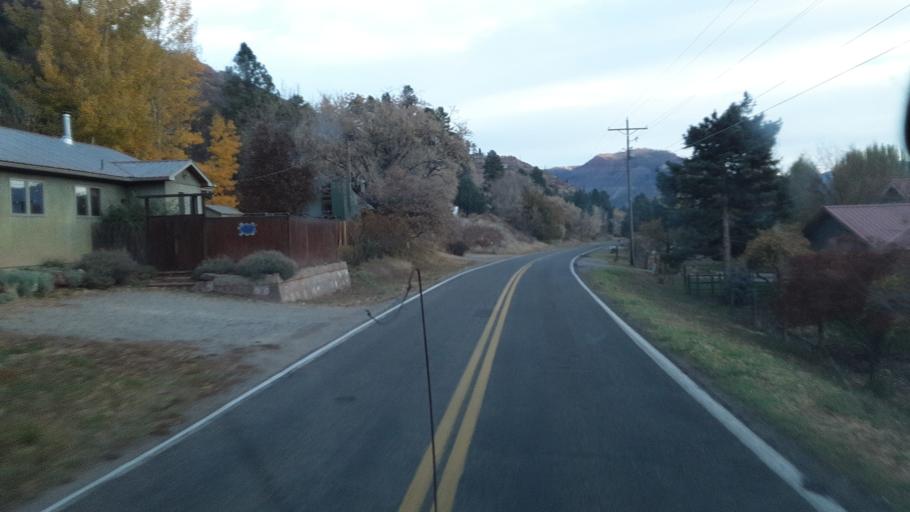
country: US
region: Colorado
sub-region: La Plata County
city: Durango
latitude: 37.3771
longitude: -107.8537
